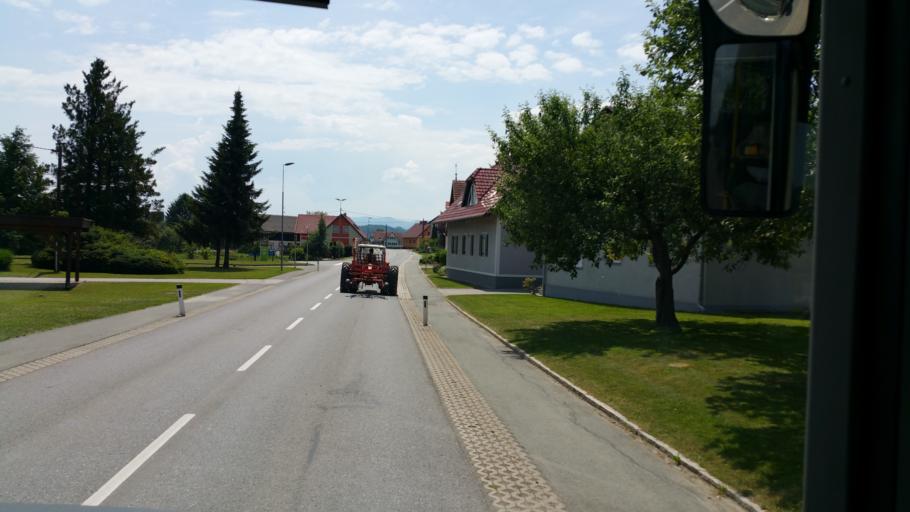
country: AT
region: Styria
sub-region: Politischer Bezirk Leibnitz
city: Pistorf
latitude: 46.7674
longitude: 15.3728
